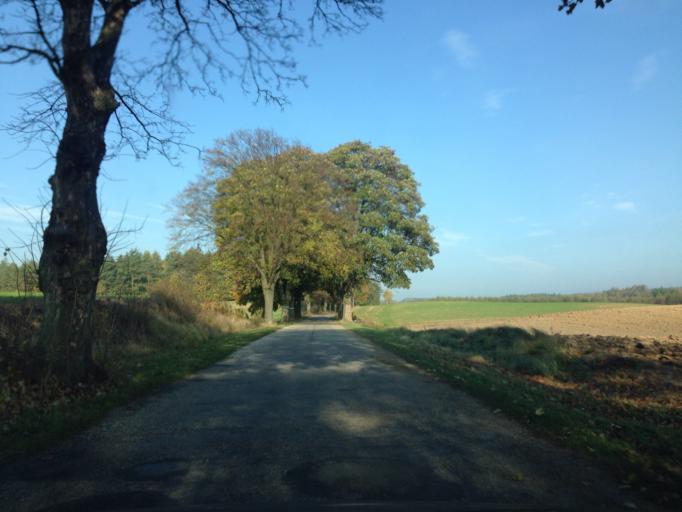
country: PL
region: Kujawsko-Pomorskie
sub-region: Powiat brodnicki
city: Gorzno
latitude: 53.2567
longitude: 19.6797
